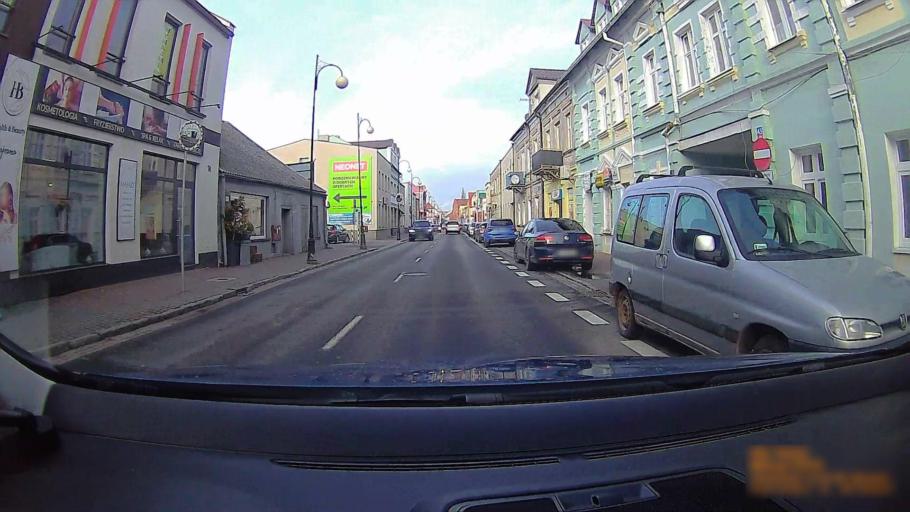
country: PL
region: Greater Poland Voivodeship
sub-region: Konin
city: Konin
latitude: 52.2056
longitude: 18.2540
